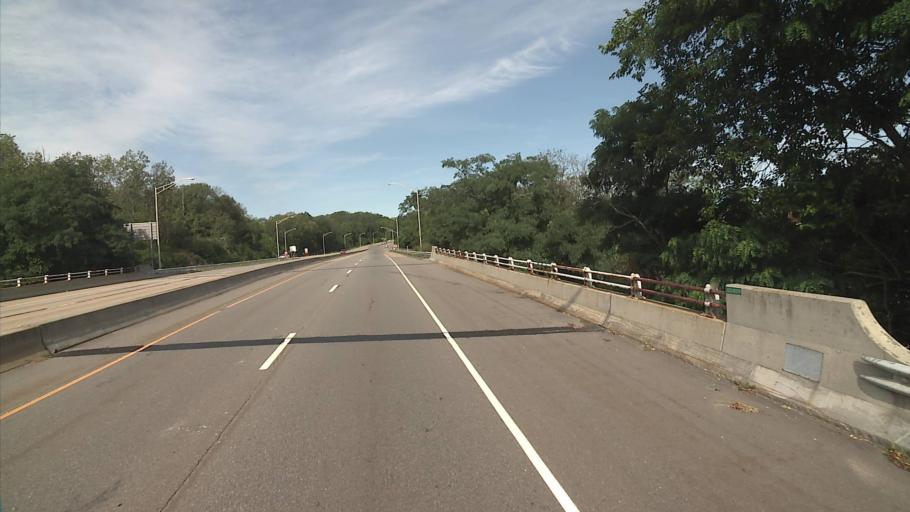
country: US
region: Connecticut
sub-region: New London County
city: Norwich
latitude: 41.5445
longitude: -72.0953
